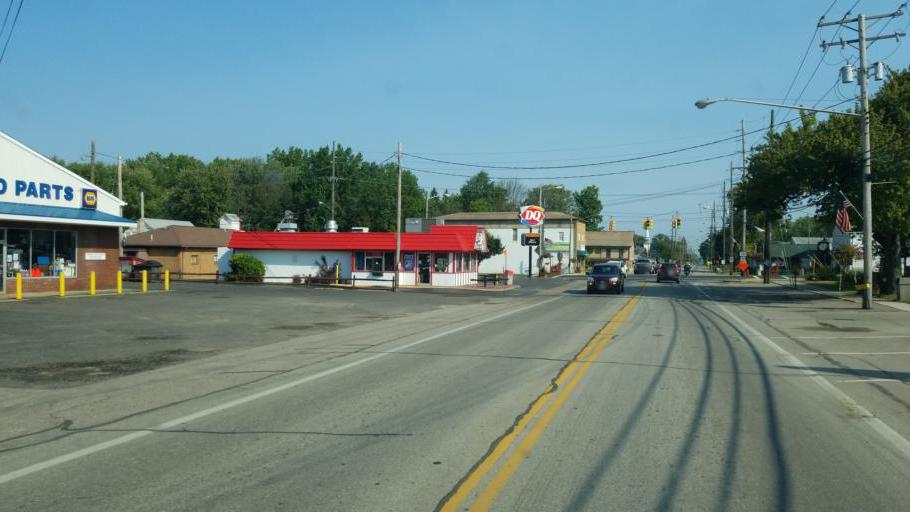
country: US
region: Ohio
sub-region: Ashtabula County
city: Orwell
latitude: 41.5344
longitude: -80.8679
